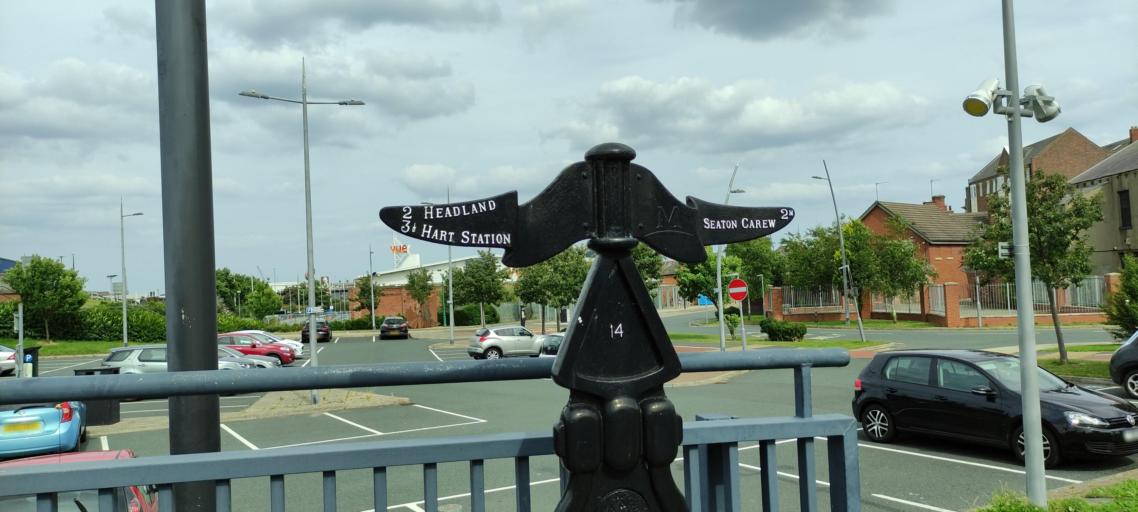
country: GB
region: England
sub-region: Hartlepool
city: Hartlepool
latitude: 54.6863
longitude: -1.2103
